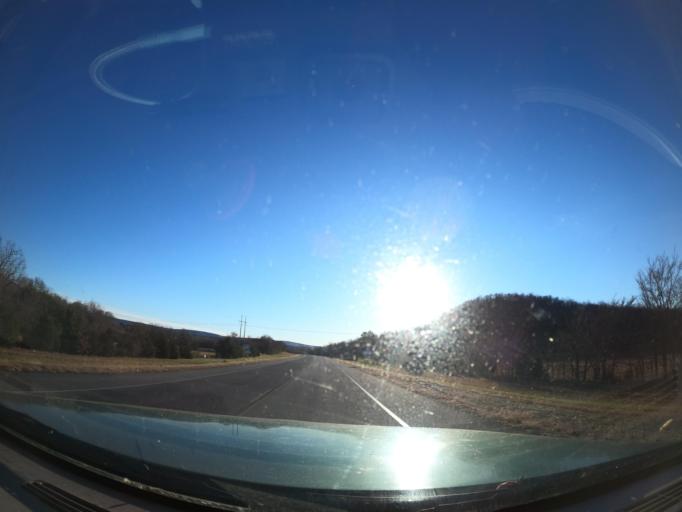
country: US
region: Oklahoma
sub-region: Pittsburg County
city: Hartshorne
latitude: 34.8592
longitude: -95.5310
